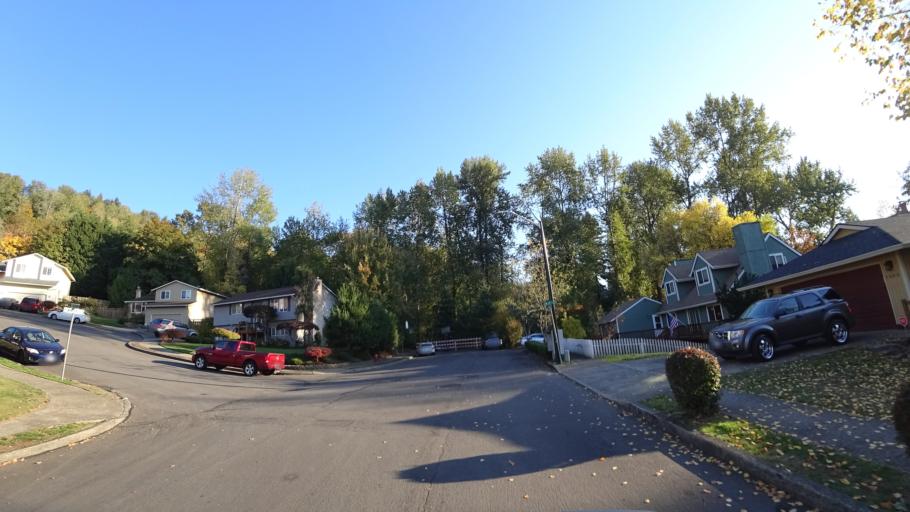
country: US
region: Oregon
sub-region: Multnomah County
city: Gresham
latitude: 45.4860
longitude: -122.4463
